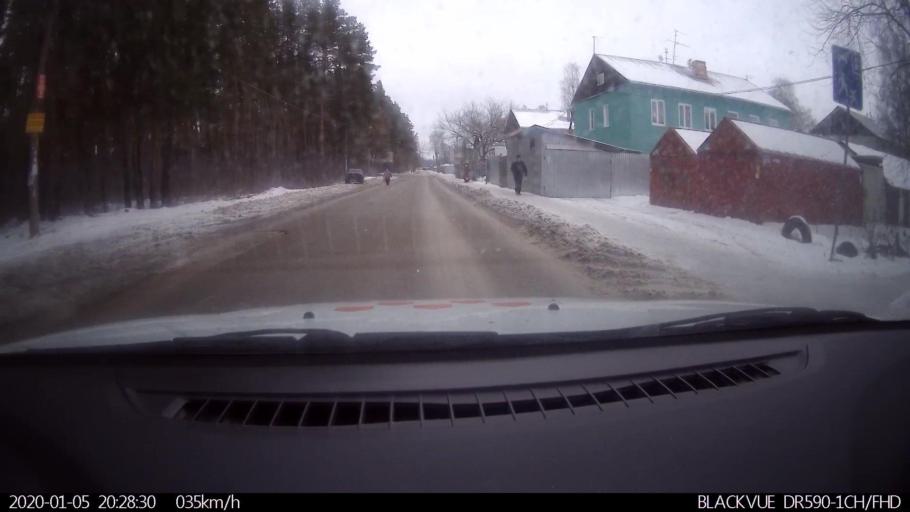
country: RU
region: Nizjnij Novgorod
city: Lukino
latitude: 56.3902
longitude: 43.7392
